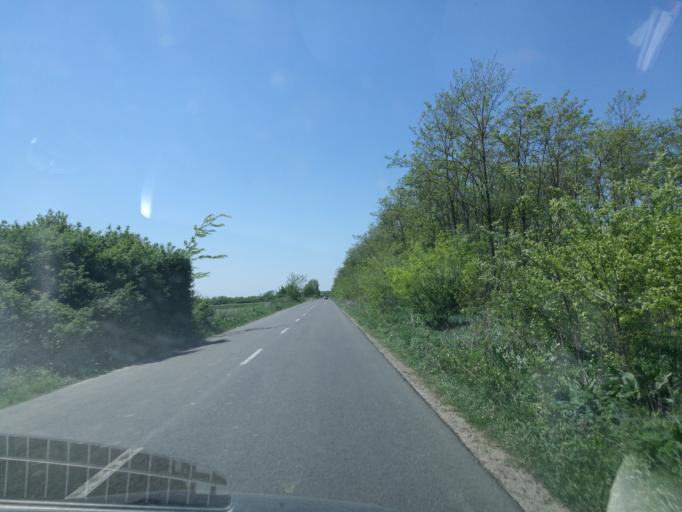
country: RO
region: Prahova
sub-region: Comuna Draganesti
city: Meri
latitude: 44.8408
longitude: 26.3162
